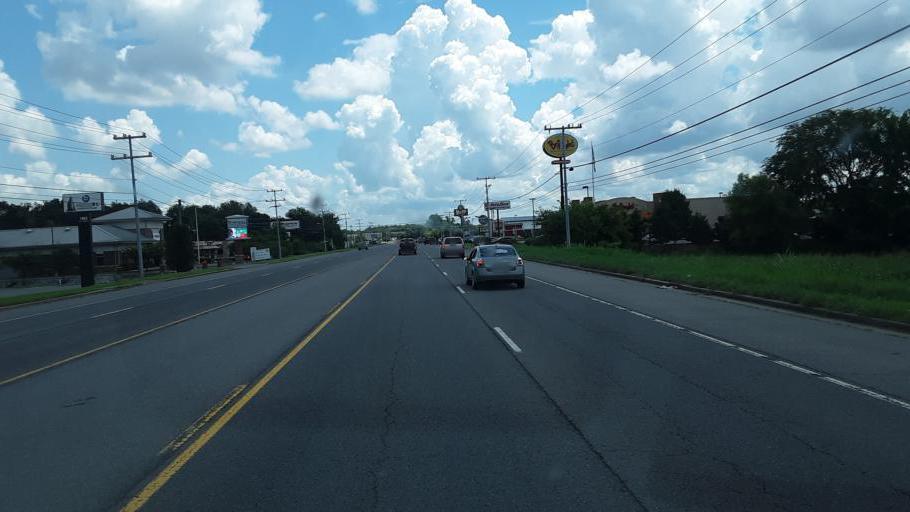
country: US
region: Tennessee
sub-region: Montgomery County
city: Clarksville
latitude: 36.6260
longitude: -87.3261
